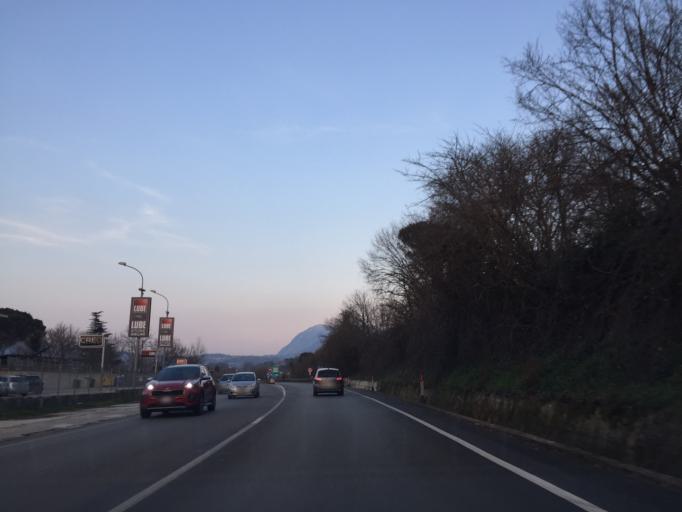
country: IT
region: Campania
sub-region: Provincia di Avellino
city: Atripalda
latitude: 40.9122
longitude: 14.8189
